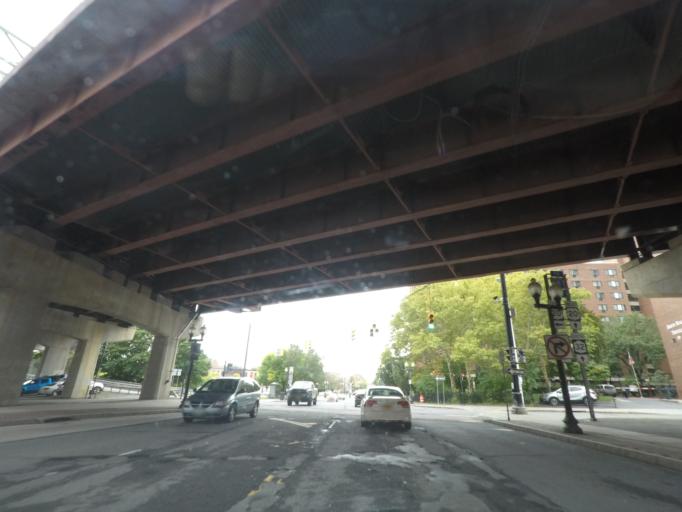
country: US
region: New York
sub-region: Albany County
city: Albany
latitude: 42.6472
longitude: -73.7543
